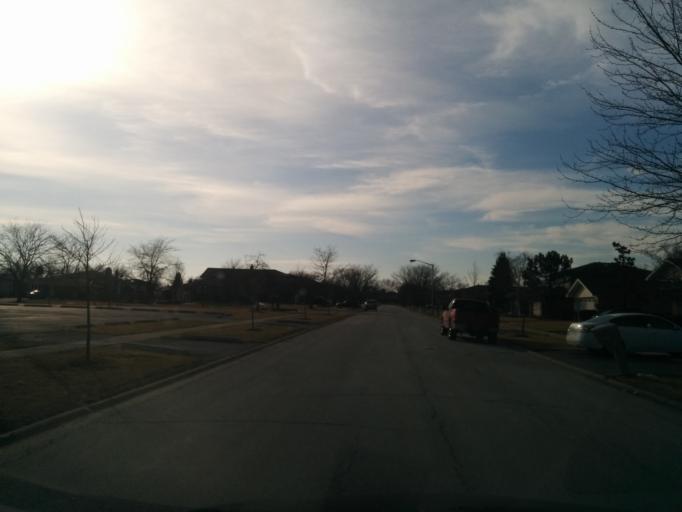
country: US
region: Illinois
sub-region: Cook County
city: Orland Hills
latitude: 41.5767
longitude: -87.8283
